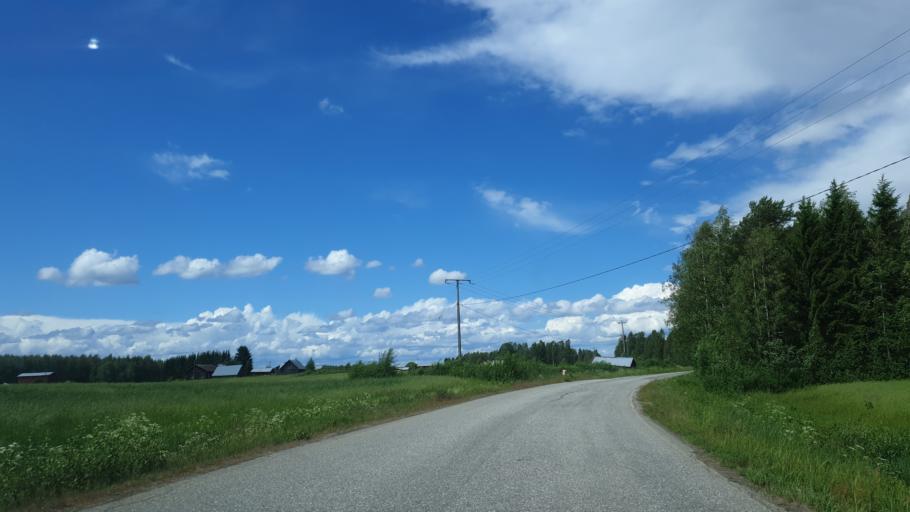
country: FI
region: Northern Savo
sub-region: Koillis-Savo
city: Kaavi
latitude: 62.9914
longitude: 28.7237
